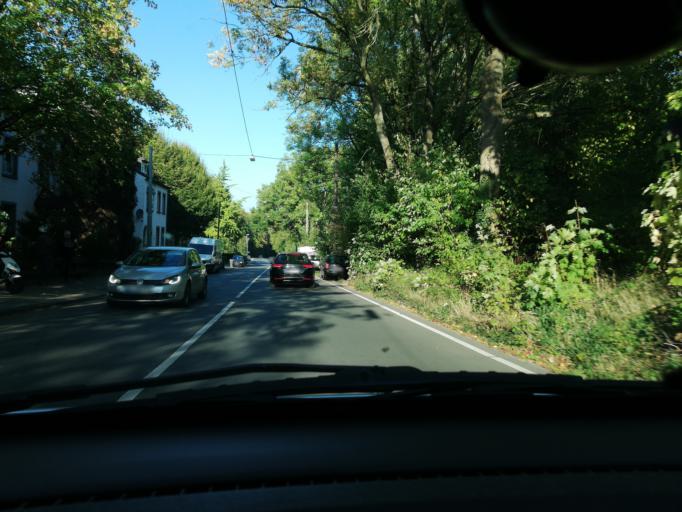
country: DE
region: North Rhine-Westphalia
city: Hattingen
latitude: 51.4022
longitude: 7.1937
